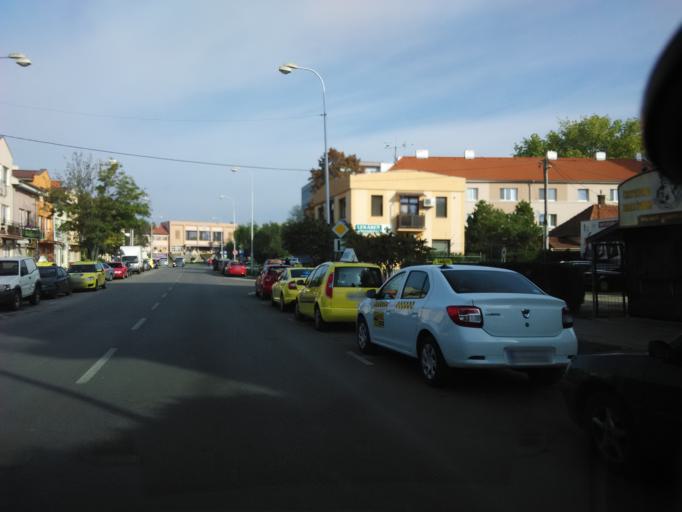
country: SK
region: Nitriansky
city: Komarno
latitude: 47.7666
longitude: 18.1256
